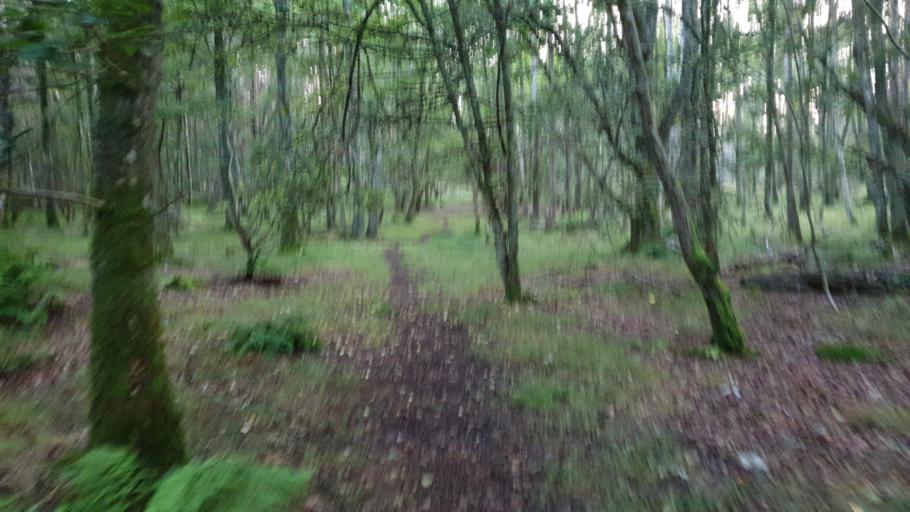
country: SE
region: Vaestra Goetaland
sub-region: Goteborg
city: Billdal
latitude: 57.5920
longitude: 11.9141
